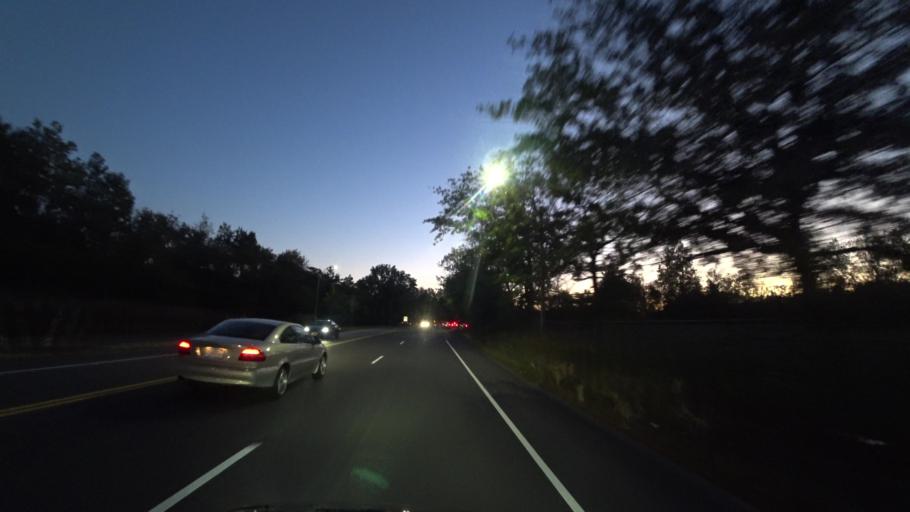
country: US
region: Massachusetts
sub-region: Middlesex County
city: Watertown
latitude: 42.3638
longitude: -71.1471
